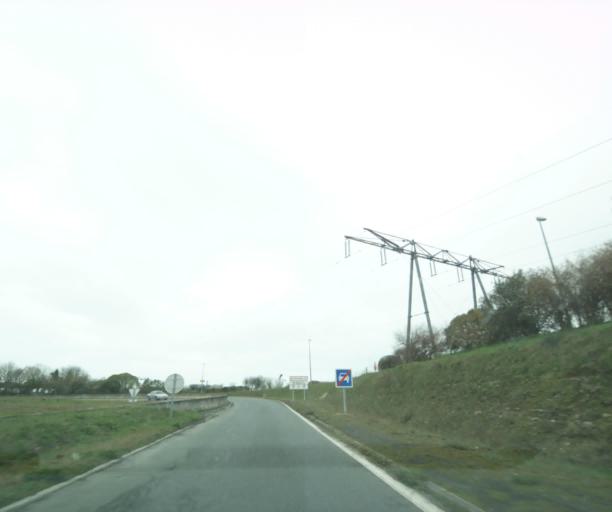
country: FR
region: Poitou-Charentes
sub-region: Departement de la Charente-Maritime
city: Lagord
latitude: 46.1745
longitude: -1.1777
